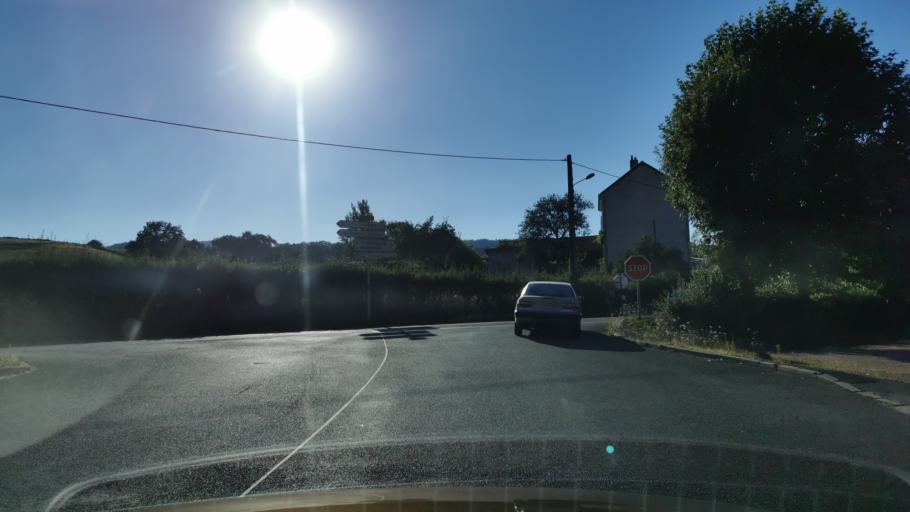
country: FR
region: Bourgogne
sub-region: Departement de Saone-et-Loire
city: Marmagne
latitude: 46.8037
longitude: 4.3297
